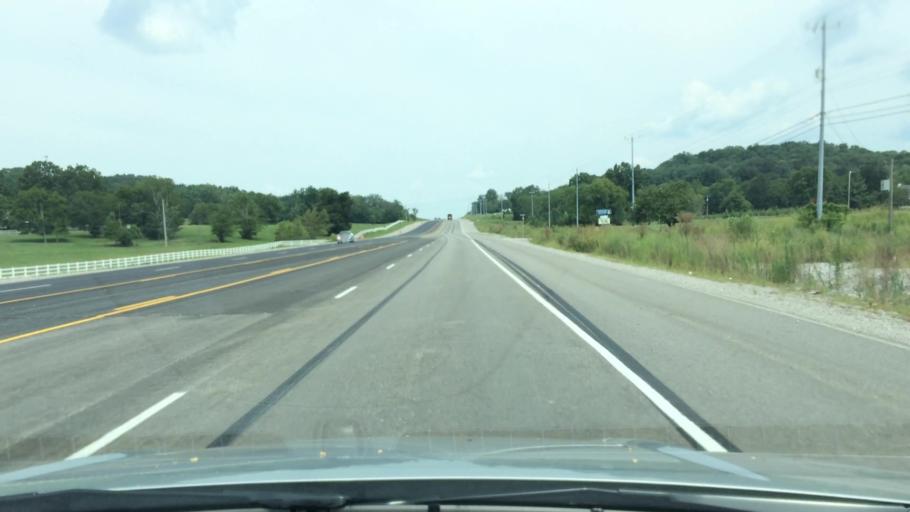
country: US
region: Tennessee
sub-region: Giles County
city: Pulaski
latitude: 35.1564
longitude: -87.0065
